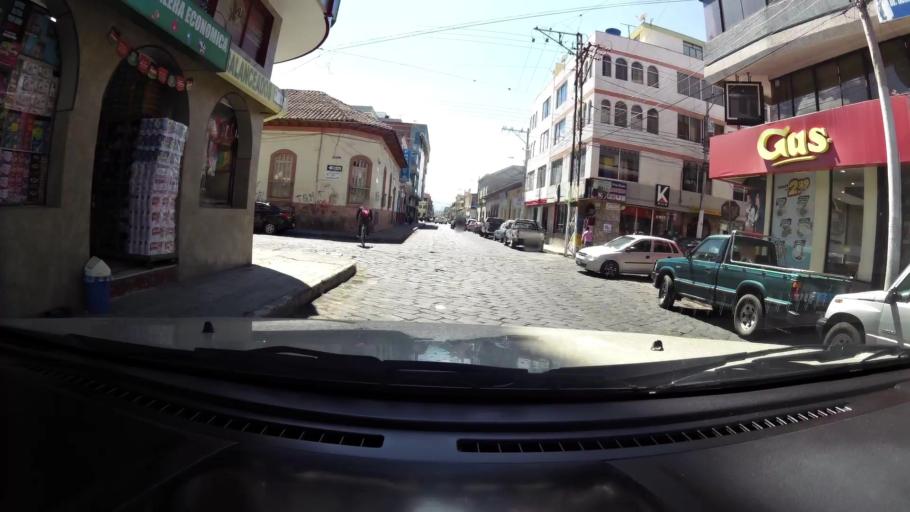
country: EC
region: Chimborazo
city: Riobamba
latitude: -1.6743
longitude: -78.6483
